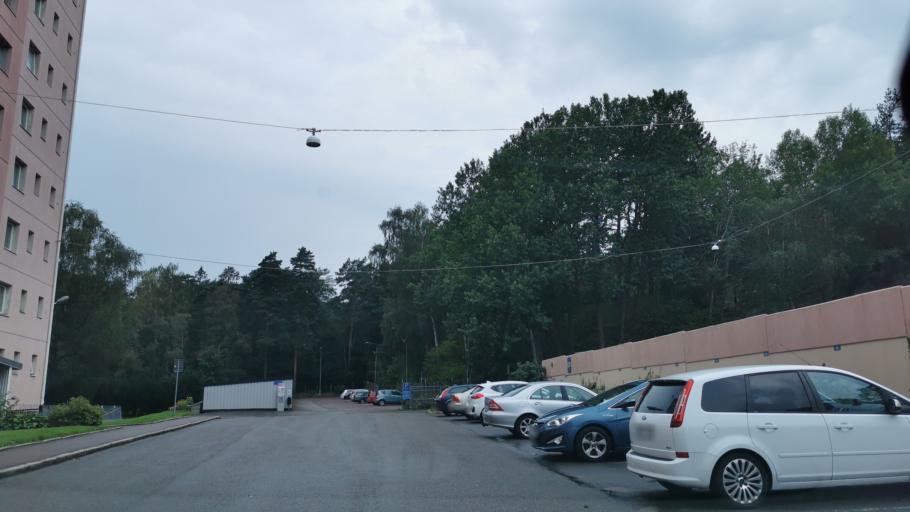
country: SE
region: Vaestra Goetaland
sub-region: Goteborg
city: Majorna
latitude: 57.6634
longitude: 11.9168
